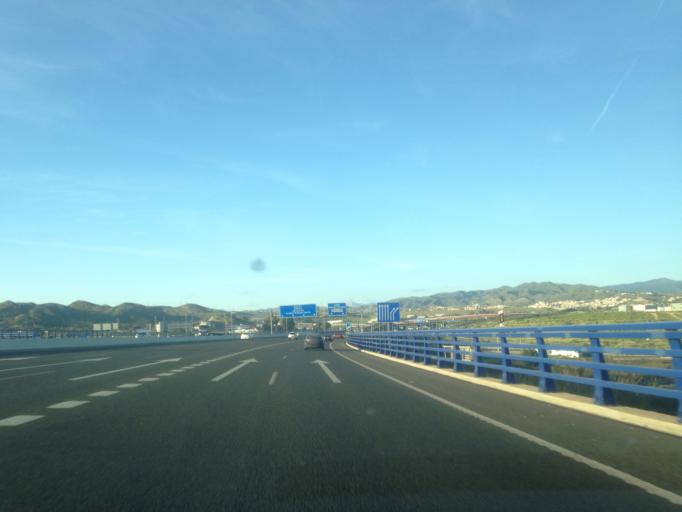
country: ES
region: Andalusia
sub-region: Provincia de Malaga
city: Alhaurin de la Torre
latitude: 36.7035
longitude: -4.5148
